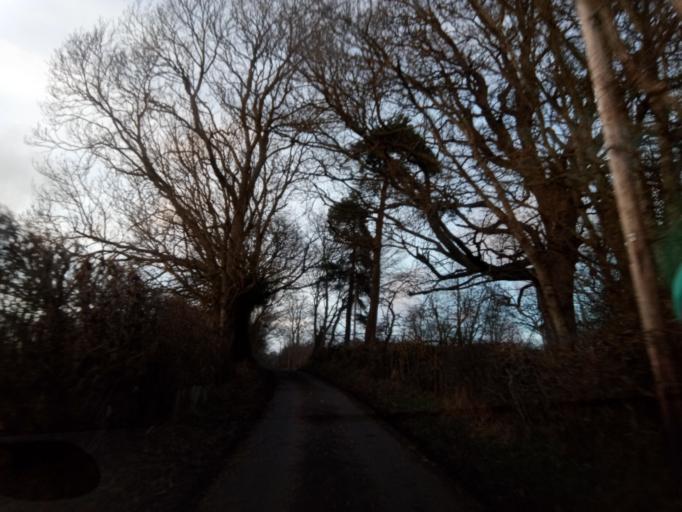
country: GB
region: Scotland
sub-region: The Scottish Borders
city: Newtown St Boswells
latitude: 55.5316
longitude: -2.7061
